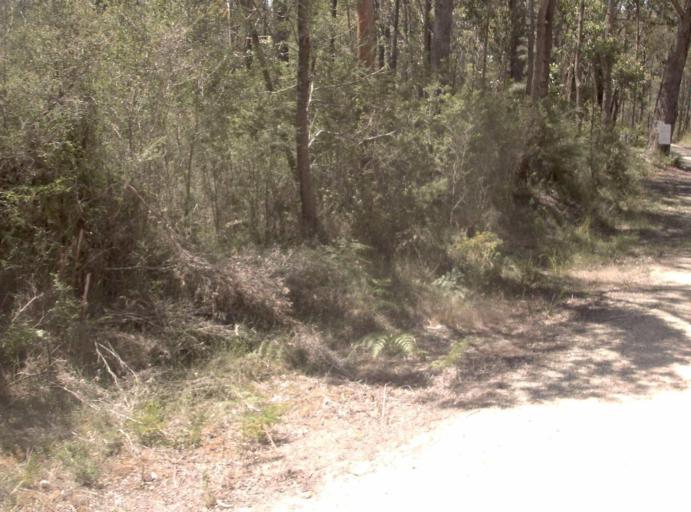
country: AU
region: New South Wales
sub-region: Bombala
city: Bombala
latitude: -37.6344
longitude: 148.8732
